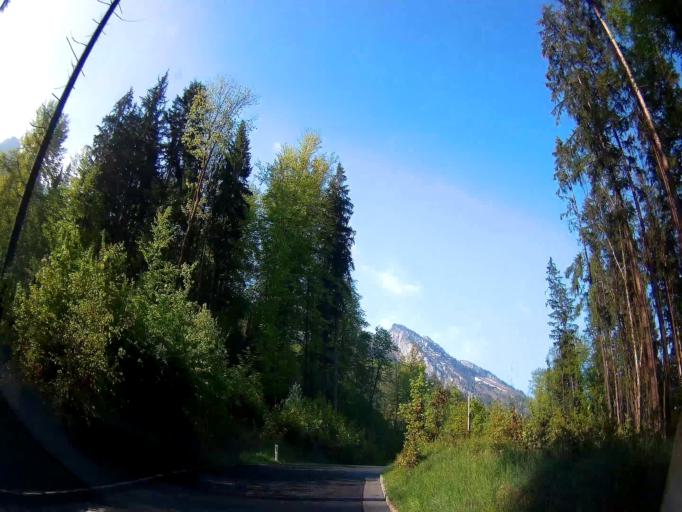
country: AT
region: Salzburg
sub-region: Politischer Bezirk Salzburg-Umgebung
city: Grodig
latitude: 47.7405
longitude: 12.9897
